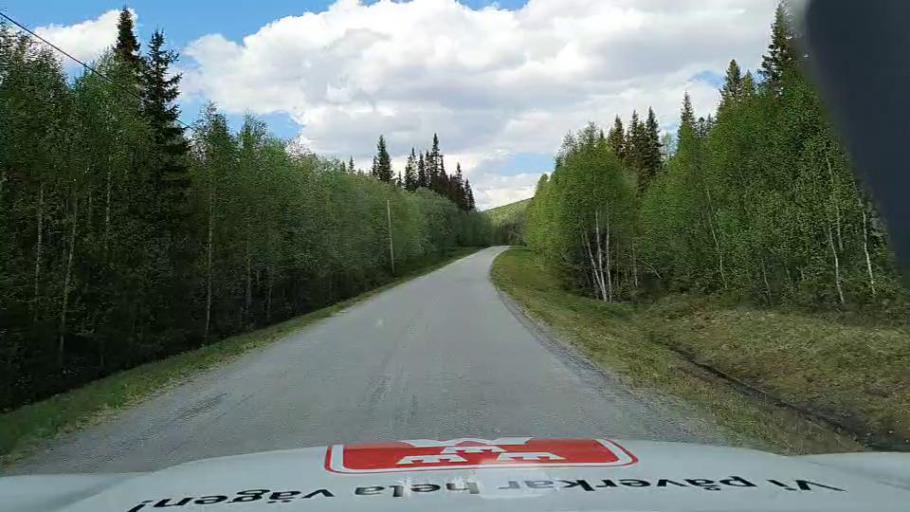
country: NO
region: Nord-Trondelag
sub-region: Lierne
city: Sandvika
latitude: 64.1287
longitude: 14.1230
